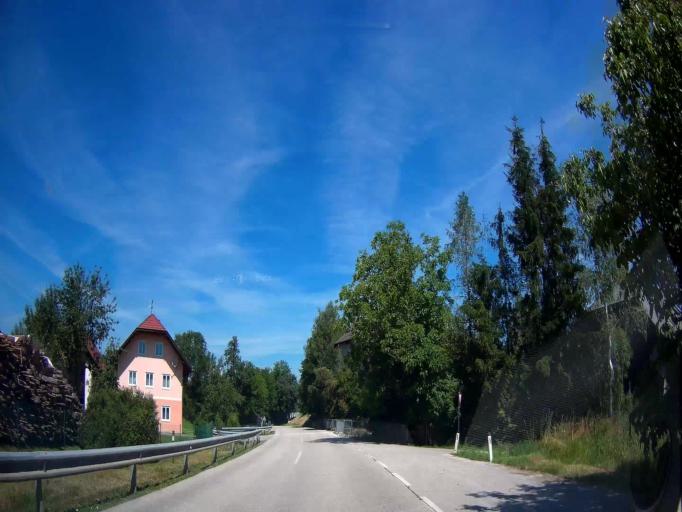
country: AT
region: Carinthia
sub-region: Politischer Bezirk Sankt Veit an der Glan
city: St. Georgen am Laengsee
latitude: 46.8008
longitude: 14.4131
